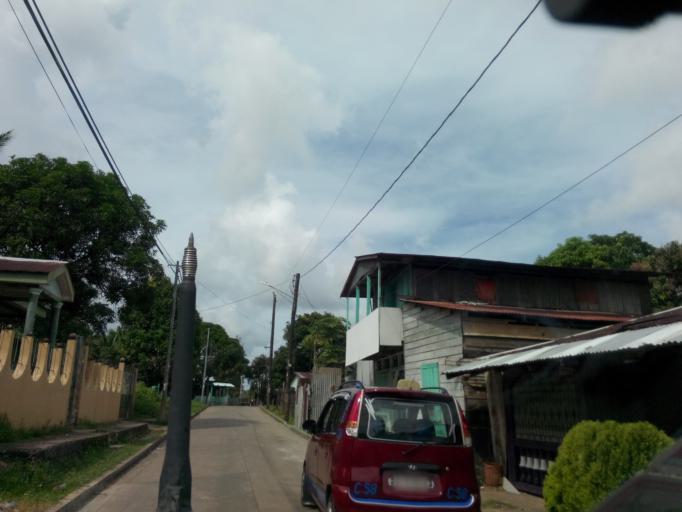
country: NI
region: Atlantico Sur
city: Bluefields
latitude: 11.9992
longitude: -83.7660
